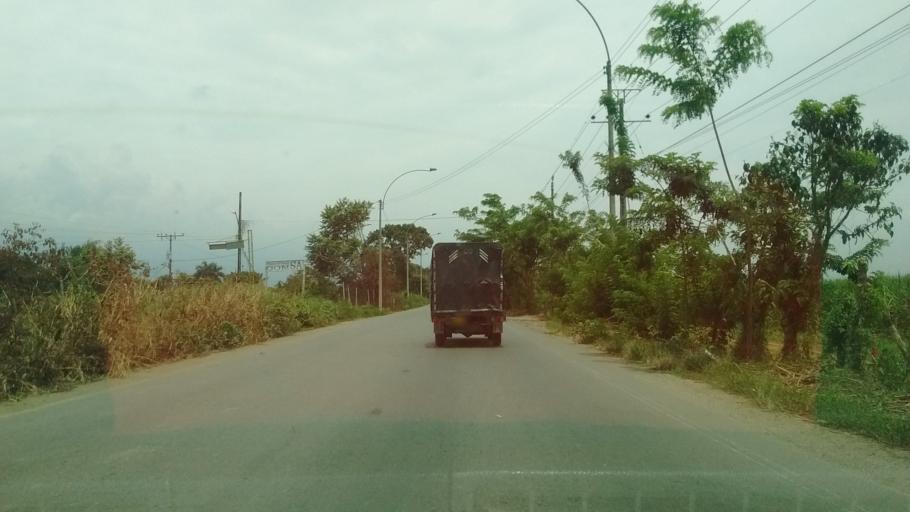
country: CO
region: Valle del Cauca
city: Jamundi
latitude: 3.3089
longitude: -76.4838
